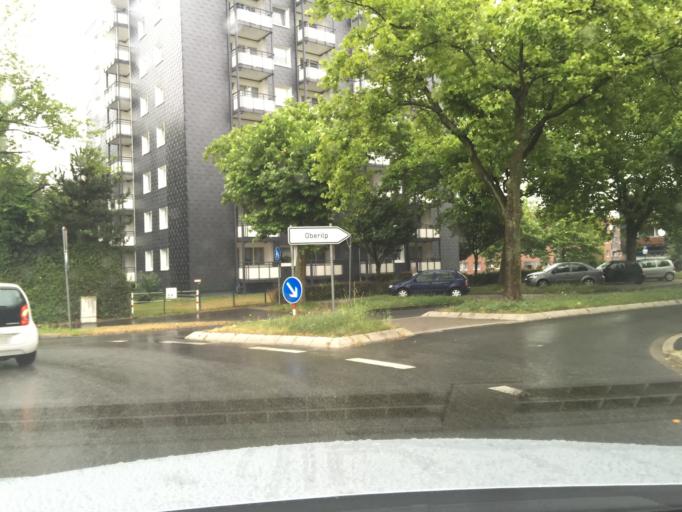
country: DE
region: North Rhine-Westphalia
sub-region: Regierungsbezirk Dusseldorf
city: Heiligenhaus
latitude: 51.3261
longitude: 6.9434
